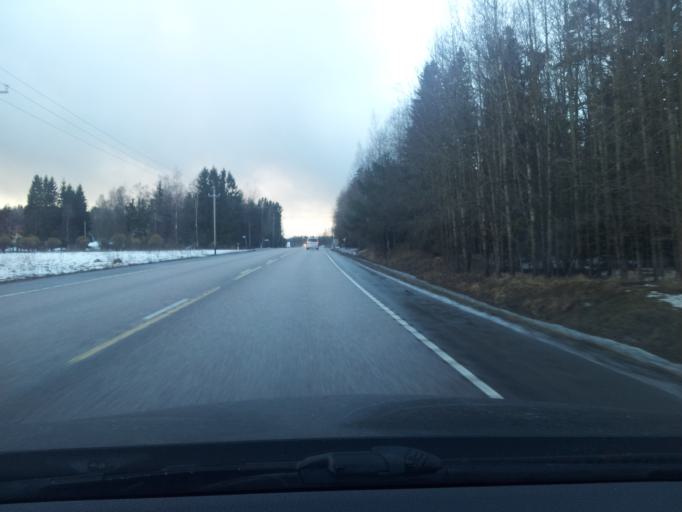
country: FI
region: Uusimaa
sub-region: Helsinki
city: Espoo
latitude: 60.1723
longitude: 24.5555
